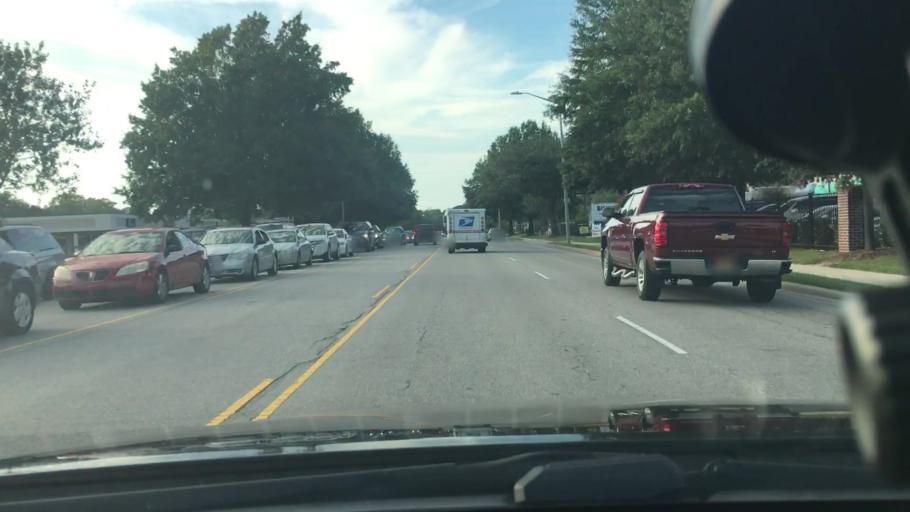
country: US
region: North Carolina
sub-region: Pitt County
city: Greenville
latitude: 35.5878
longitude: -77.3734
